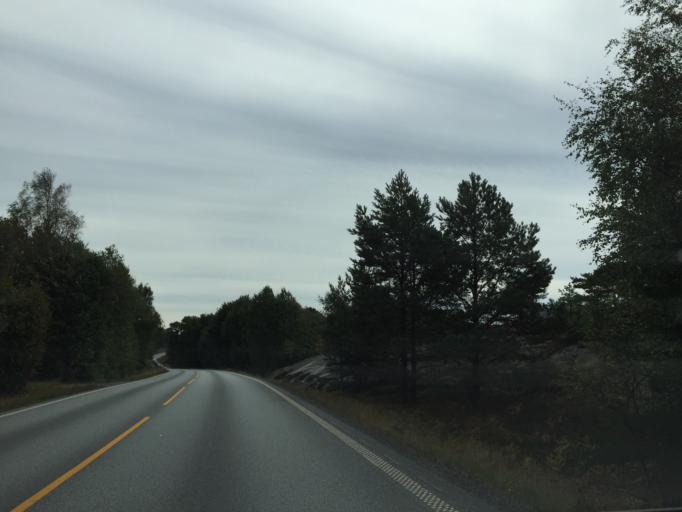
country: NO
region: Ostfold
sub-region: Hvaler
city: Skjaerhalden
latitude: 59.0624
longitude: 10.9400
